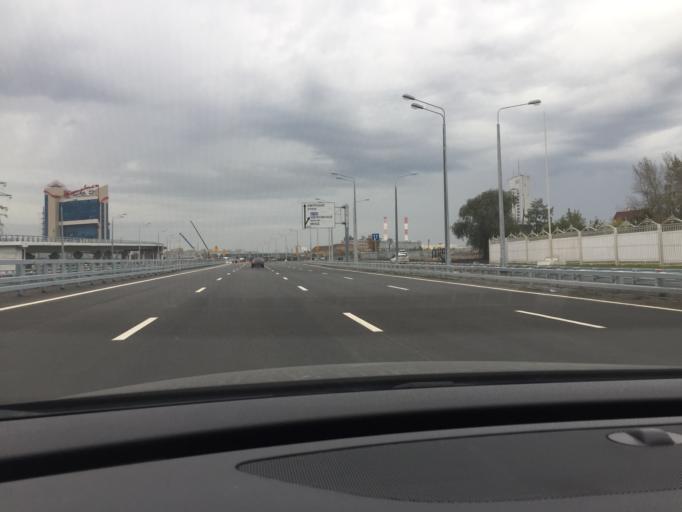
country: RU
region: Moskovskaya
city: Bogorodskoye
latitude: 55.7965
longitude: 37.7478
